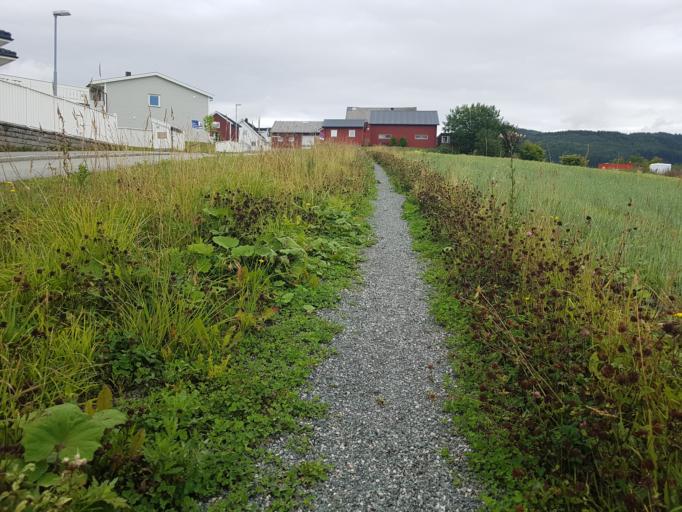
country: NO
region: Sor-Trondelag
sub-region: Trondheim
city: Trondheim
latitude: 63.3838
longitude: 10.4251
